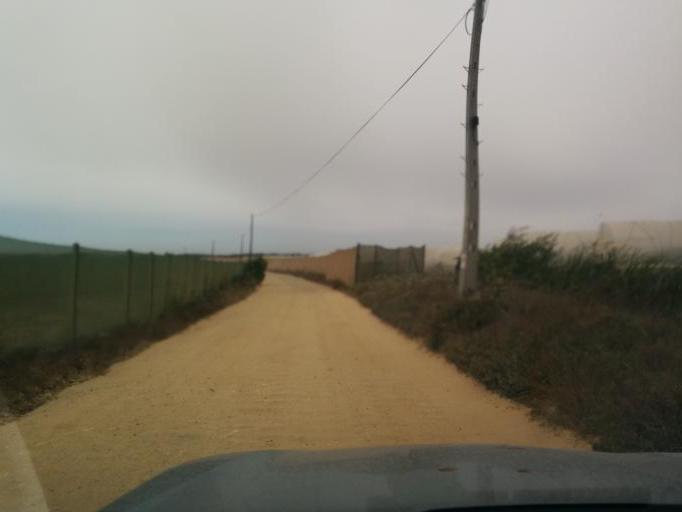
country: PT
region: Beja
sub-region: Odemira
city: Sao Teotonio
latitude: 37.5139
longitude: -8.7835
